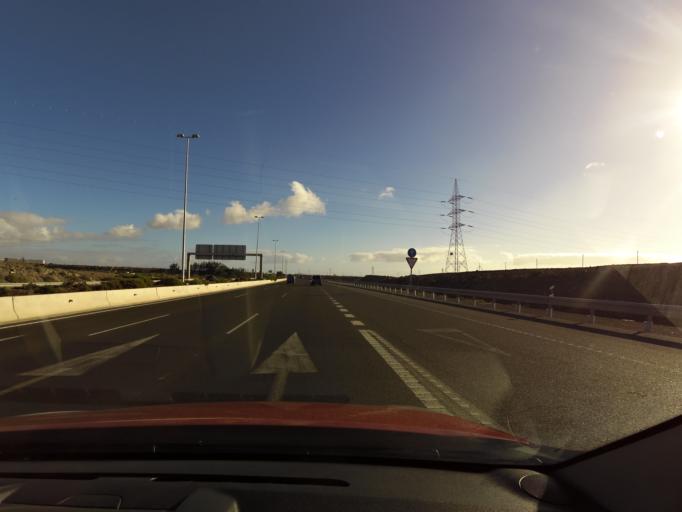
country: ES
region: Canary Islands
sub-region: Provincia de Las Palmas
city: Cruce de Arinaga
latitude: 27.8252
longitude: -15.4541
